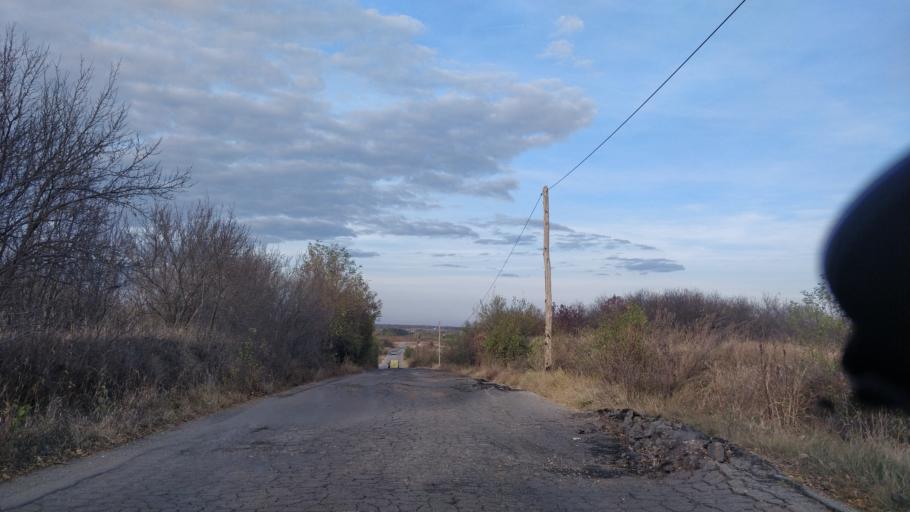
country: RO
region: Giurgiu
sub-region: Comuna Bucsani
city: Bucsani
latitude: 44.3536
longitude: 25.6570
